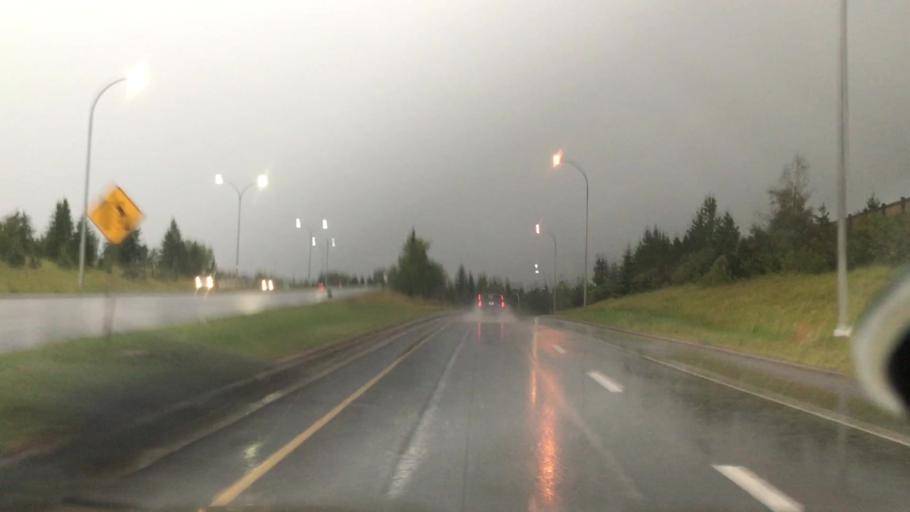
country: CA
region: Alberta
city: Edmonton
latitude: 53.4801
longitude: -113.5717
